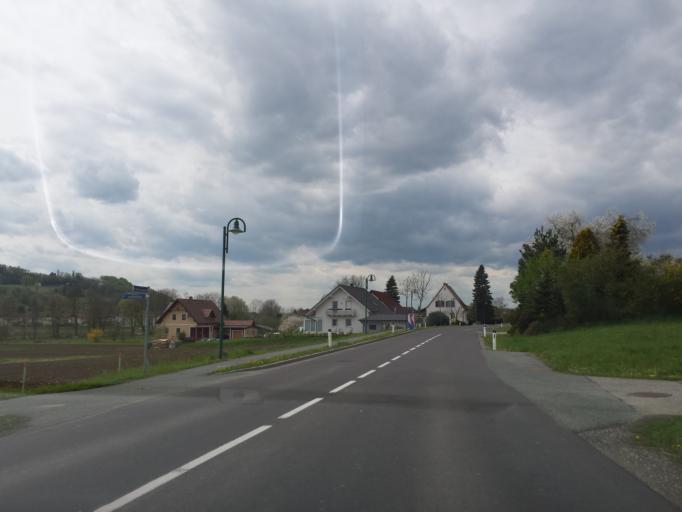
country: AT
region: Styria
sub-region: Politischer Bezirk Hartberg-Fuerstenfeld
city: Loipersdorf bei Fuerstenfeld
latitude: 47.0152
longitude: 16.1108
